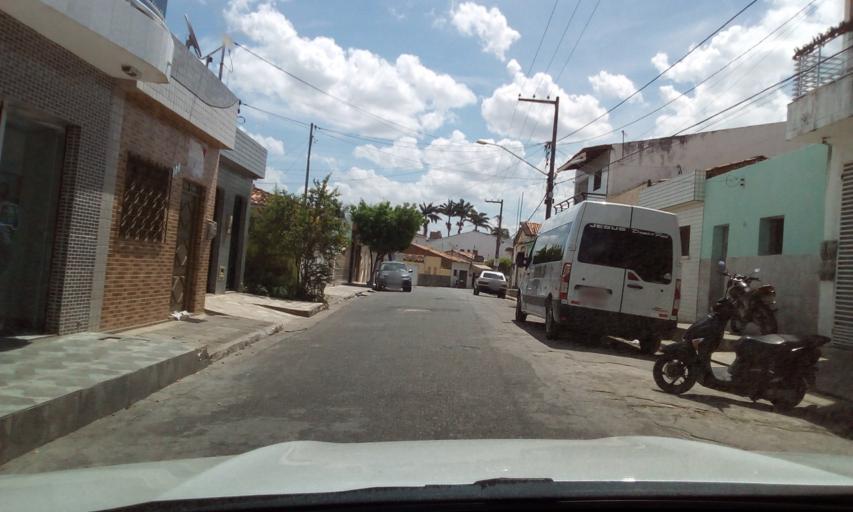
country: BR
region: Paraiba
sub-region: Guarabira
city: Guarabira
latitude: -6.8482
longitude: -35.4870
